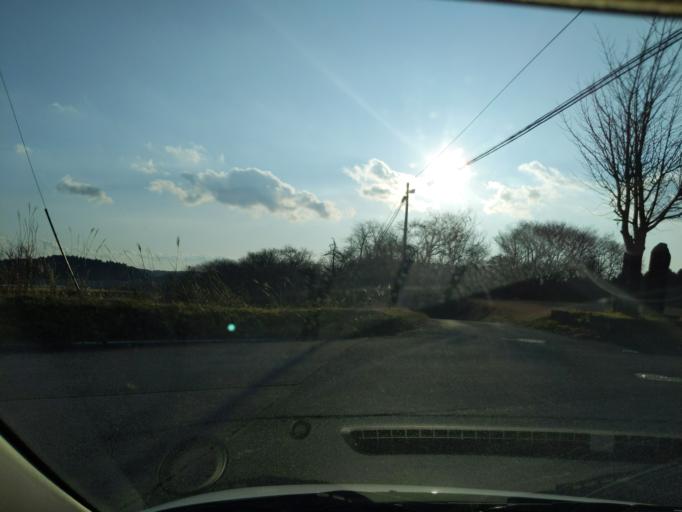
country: JP
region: Miyagi
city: Wakuya
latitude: 38.6944
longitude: 141.1068
